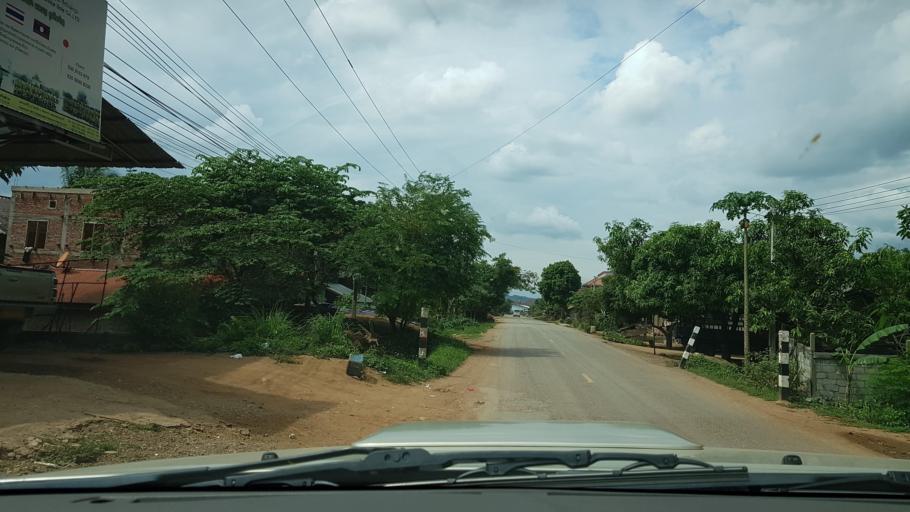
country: LA
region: Loungnamtha
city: Muang Nale
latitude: 20.2919
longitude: 101.6332
